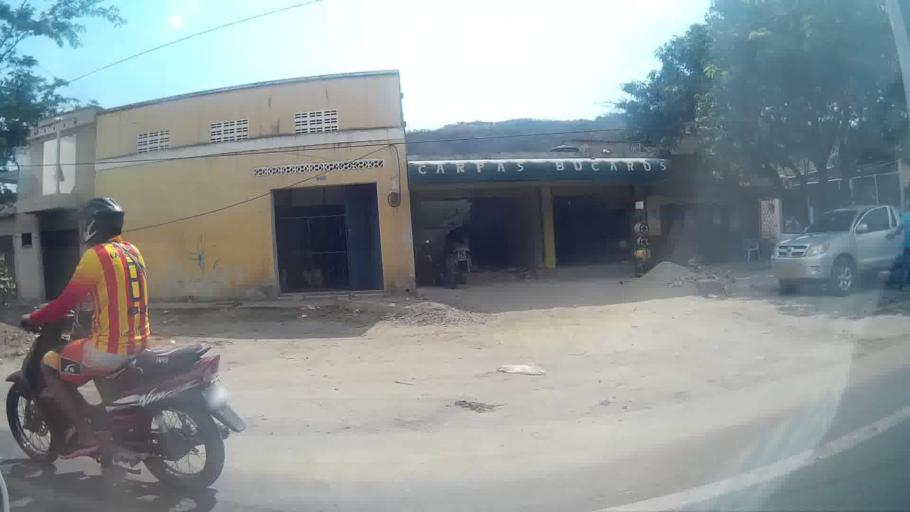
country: CO
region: Magdalena
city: Santa Marta
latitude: 11.2101
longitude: -74.1922
